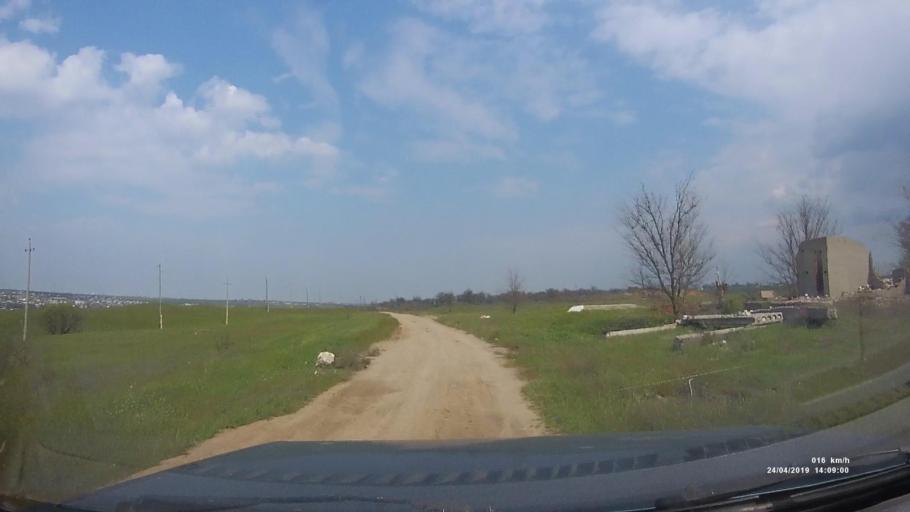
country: RU
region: Kalmykiya
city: Arshan'
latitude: 46.2637
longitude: 44.2205
